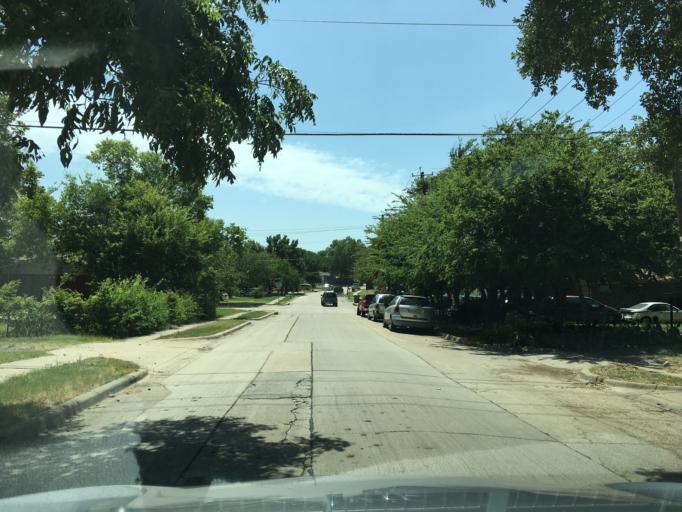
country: US
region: Texas
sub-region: Dallas County
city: Garland
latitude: 32.8930
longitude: -96.6260
